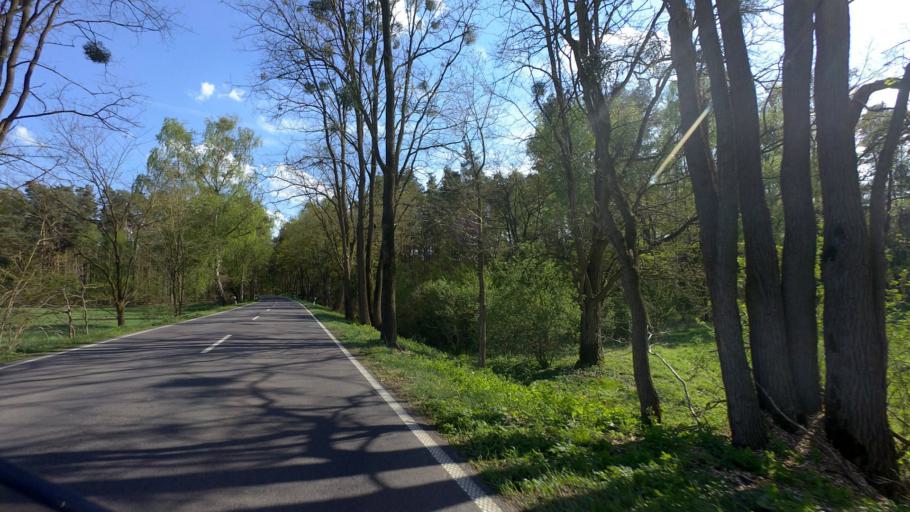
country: DE
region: Brandenburg
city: Templin
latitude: 53.0587
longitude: 13.5223
